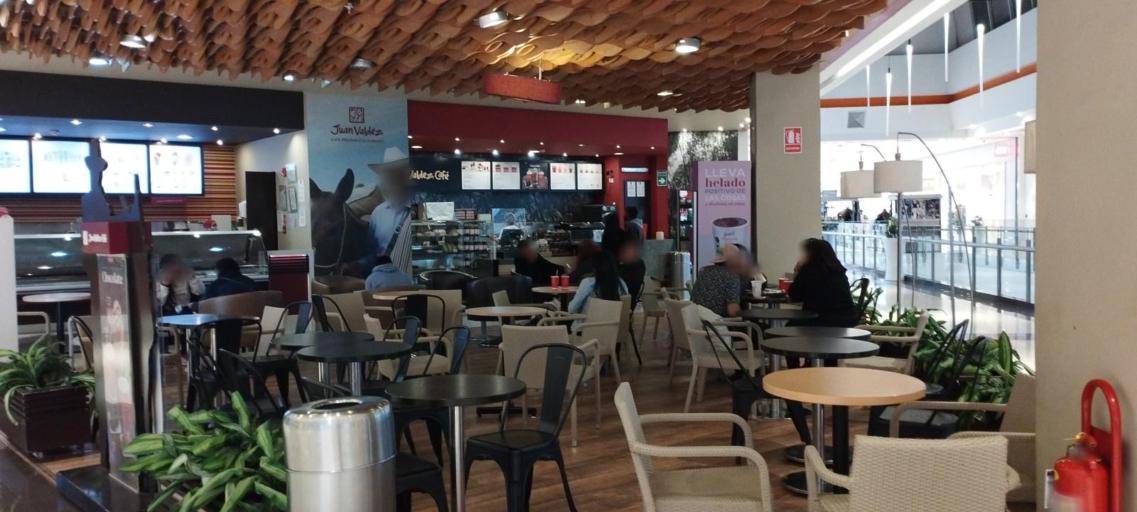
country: PE
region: Cusco
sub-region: Provincia de Cusco
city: Cusco
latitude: -13.5239
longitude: -71.9502
